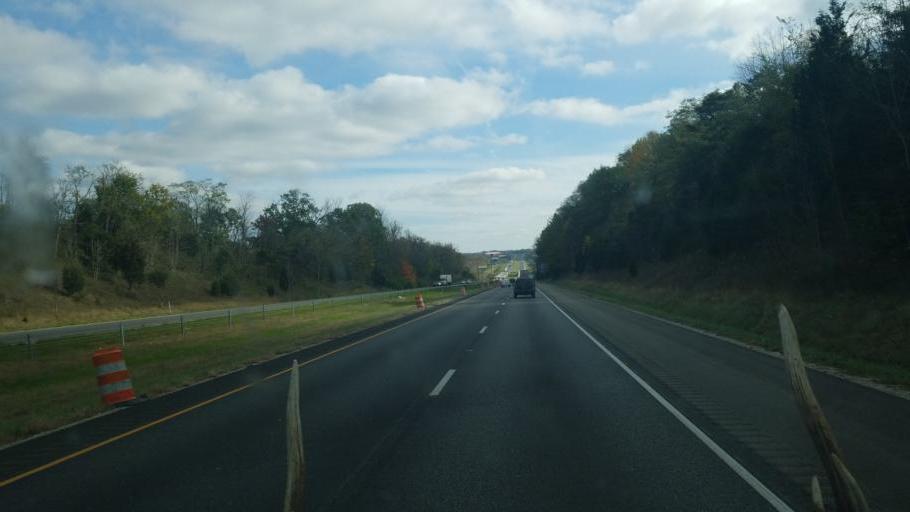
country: US
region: Ohio
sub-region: Preble County
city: New Paris
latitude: 39.8538
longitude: -84.8390
